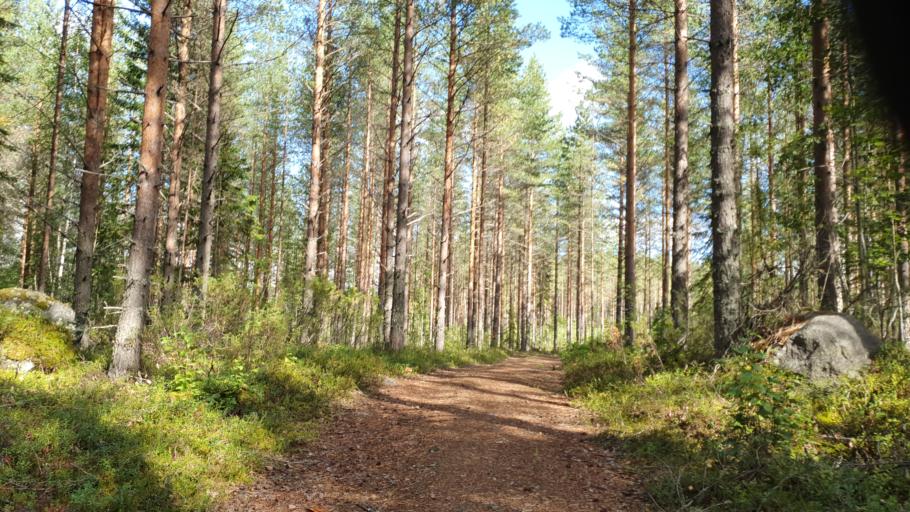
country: FI
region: Kainuu
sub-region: Kehys-Kainuu
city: Kuhmo
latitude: 64.1466
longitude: 29.3412
